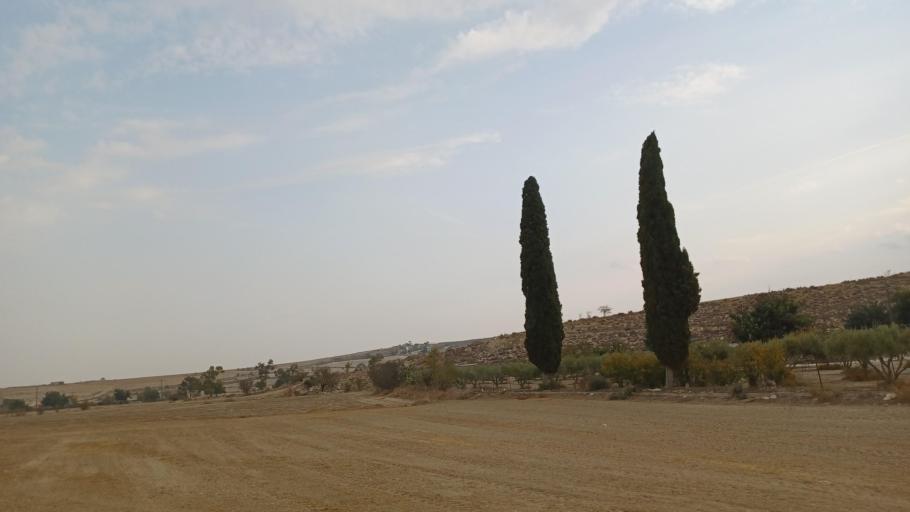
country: CY
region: Larnaka
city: Athienou
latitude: 35.0316
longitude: 33.5720
